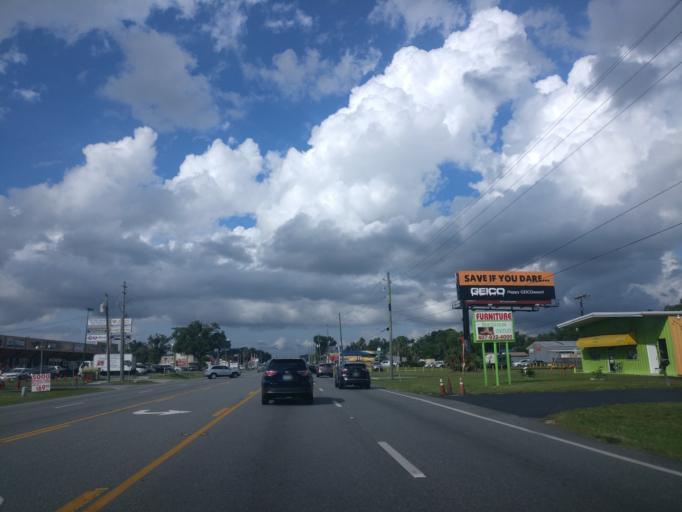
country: US
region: Florida
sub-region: Osceola County
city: Kissimmee
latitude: 28.3230
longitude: -81.4037
